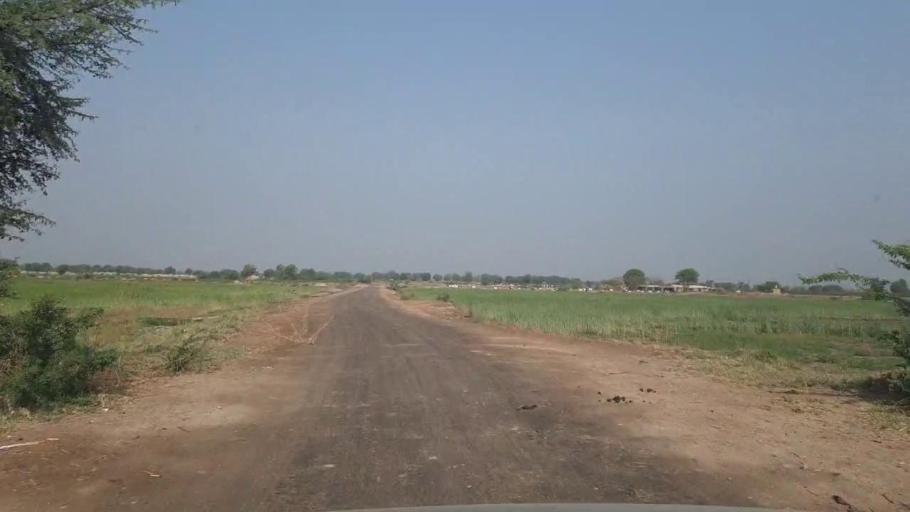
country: PK
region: Sindh
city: Umarkot
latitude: 25.4118
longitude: 69.6838
